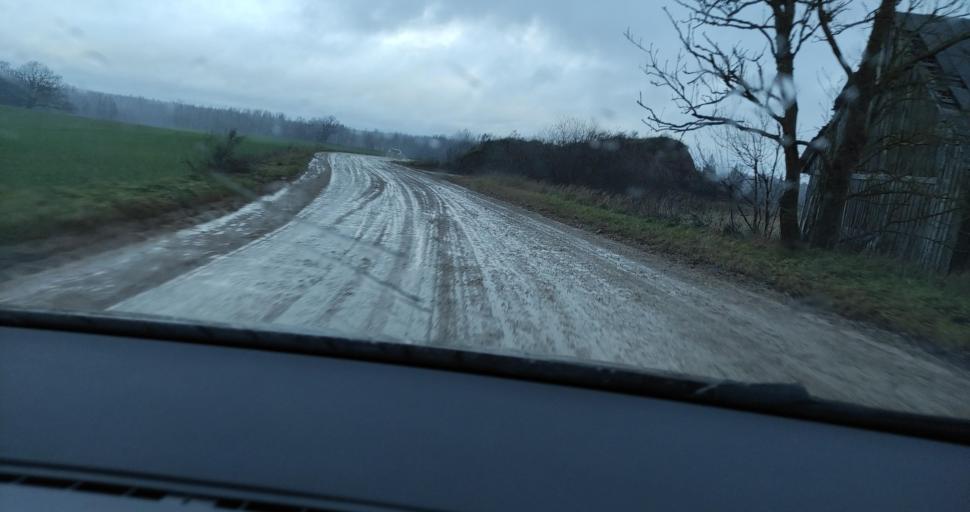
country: LV
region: Skrunda
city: Skrunda
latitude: 56.7010
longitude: 22.2116
